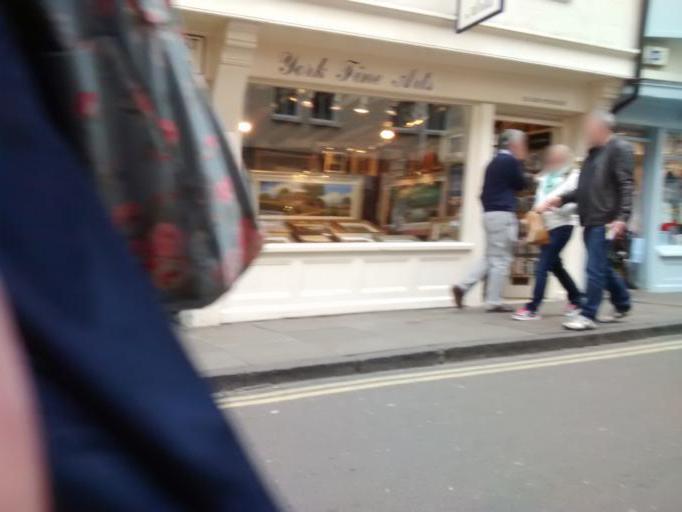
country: GB
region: England
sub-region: City of York
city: York
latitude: 53.9607
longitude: -1.0809
